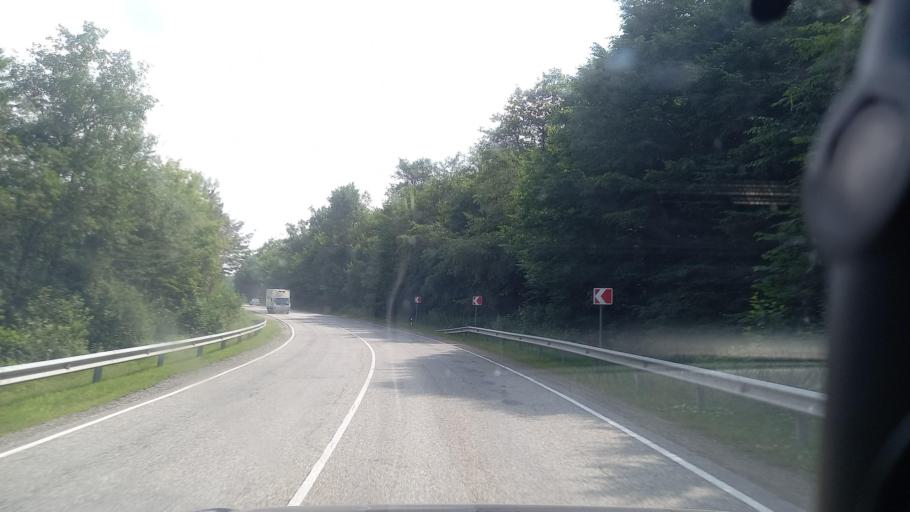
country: RU
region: Karachayevo-Cherkesiya
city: Kurdzhinovo
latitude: 44.0359
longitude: 40.8952
